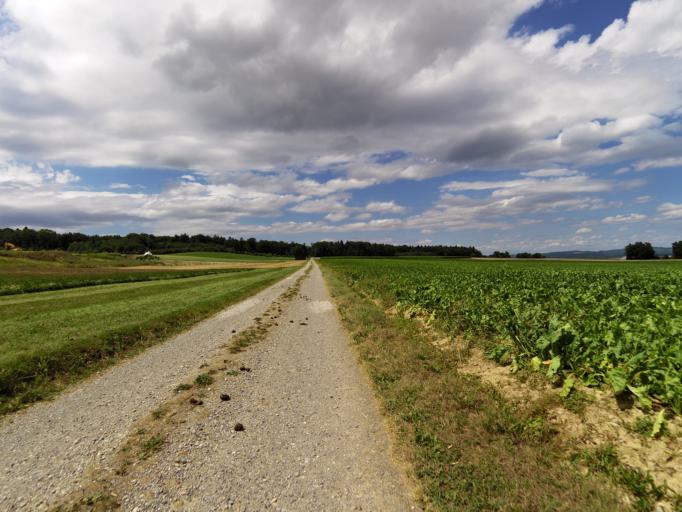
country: CH
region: Thurgau
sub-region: Kreuzlingen District
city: Ermatingen
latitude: 47.6498
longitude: 9.0874
